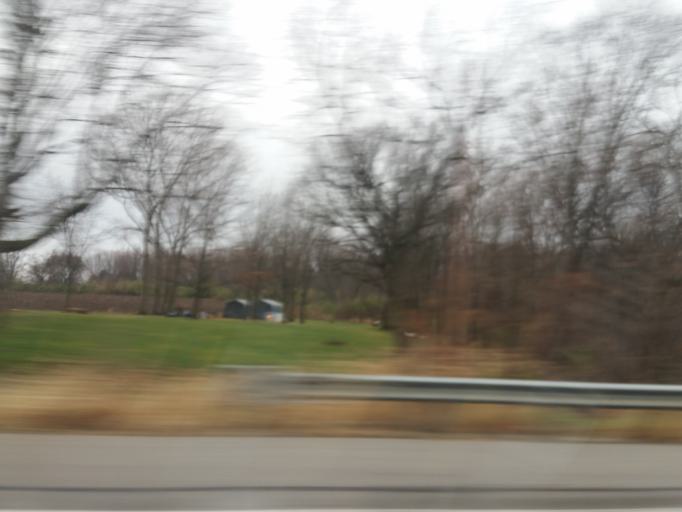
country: US
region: Iowa
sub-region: Black Hawk County
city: Elk Run Heights
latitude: 42.3871
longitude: -92.2474
